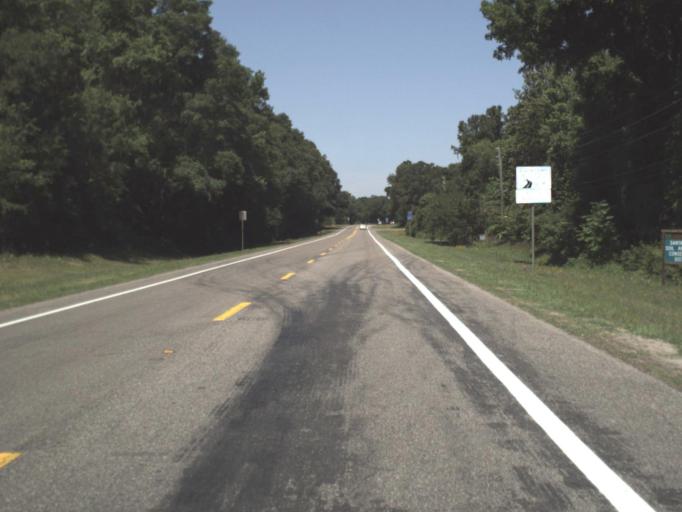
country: US
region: Florida
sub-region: Suwannee County
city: Wellborn
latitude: 30.2035
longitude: -82.7951
